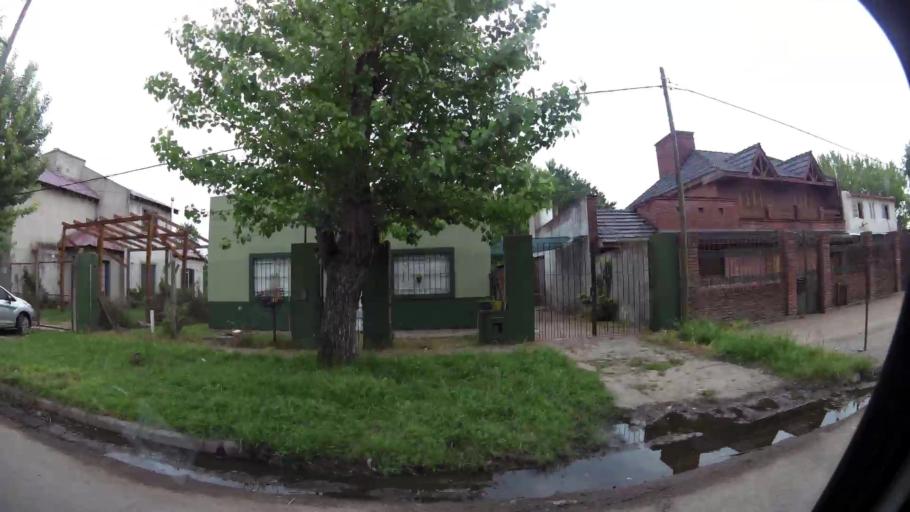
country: AR
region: Buenos Aires
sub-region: Partido de La Plata
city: La Plata
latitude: -34.9181
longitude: -58.0109
